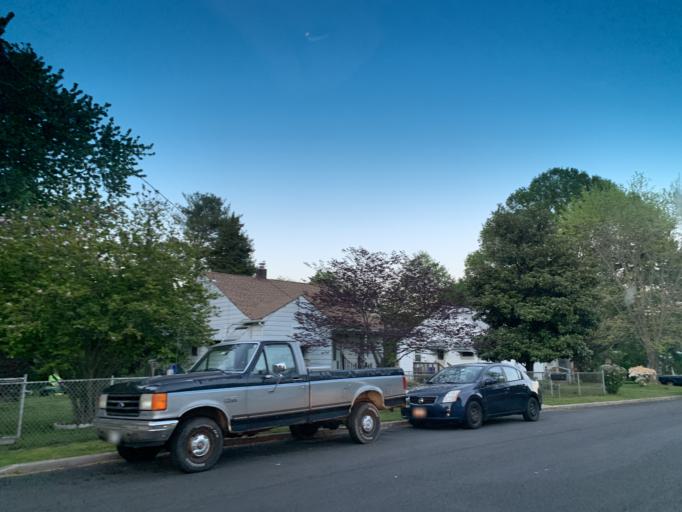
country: US
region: Maryland
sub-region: Harford County
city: Aberdeen
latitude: 39.5078
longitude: -76.1757
